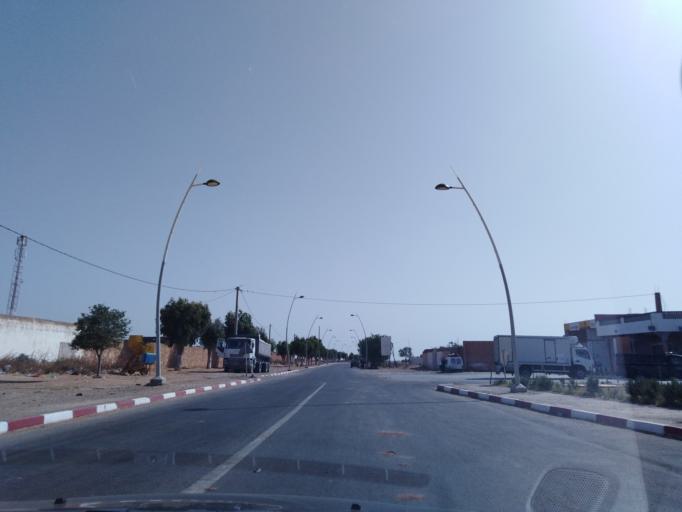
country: MA
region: Doukkala-Abda
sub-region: Safi
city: Safi
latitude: 32.2532
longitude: -8.9831
